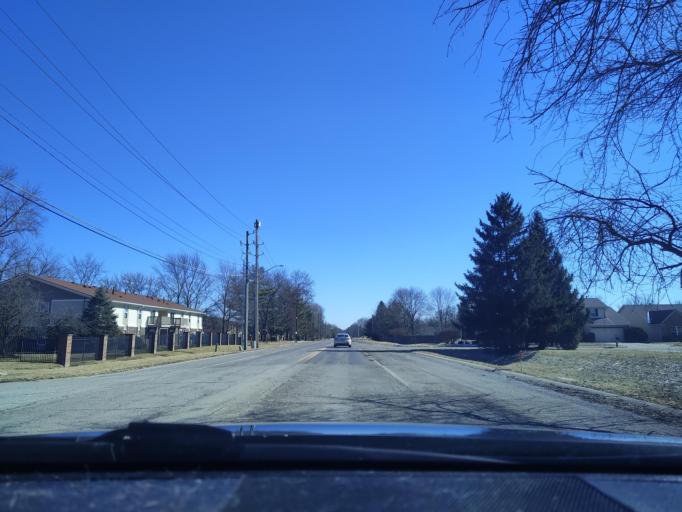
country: US
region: Indiana
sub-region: Marion County
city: Meridian Hills
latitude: 39.8974
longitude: -86.1982
